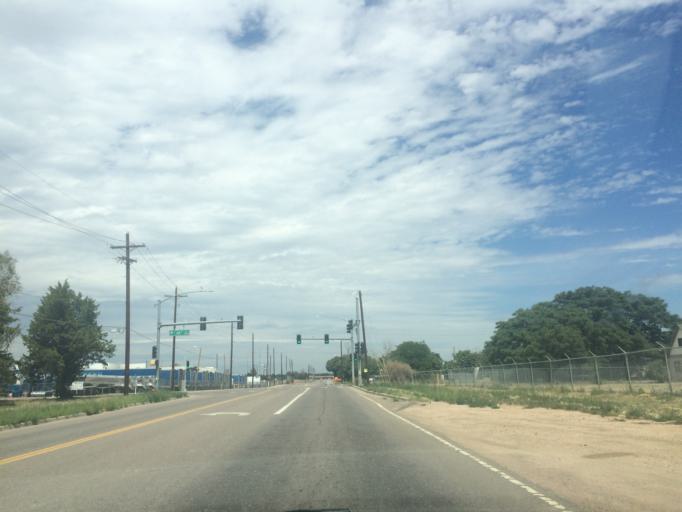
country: US
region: Colorado
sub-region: Adams County
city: Welby
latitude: 39.8157
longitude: -104.9592
